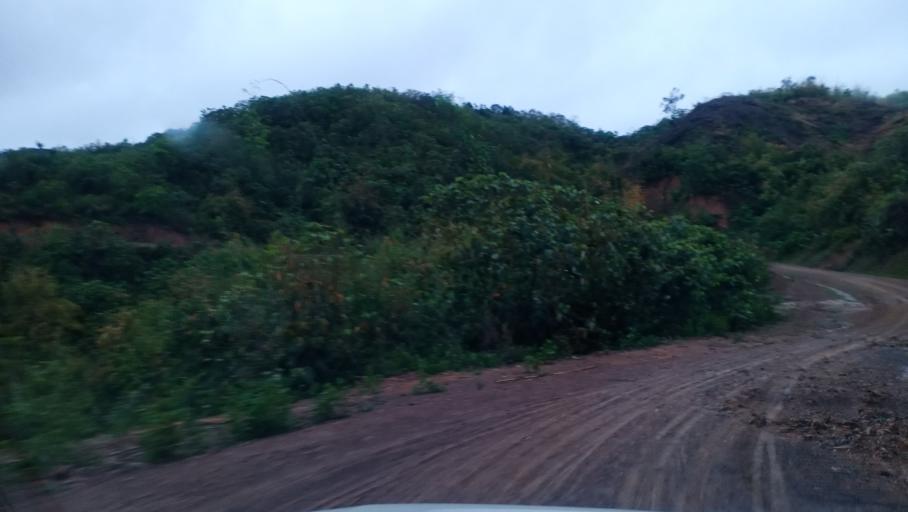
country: VN
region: Huyen Dien Bien
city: Dien Bien Phu
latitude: 21.3474
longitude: 102.7193
